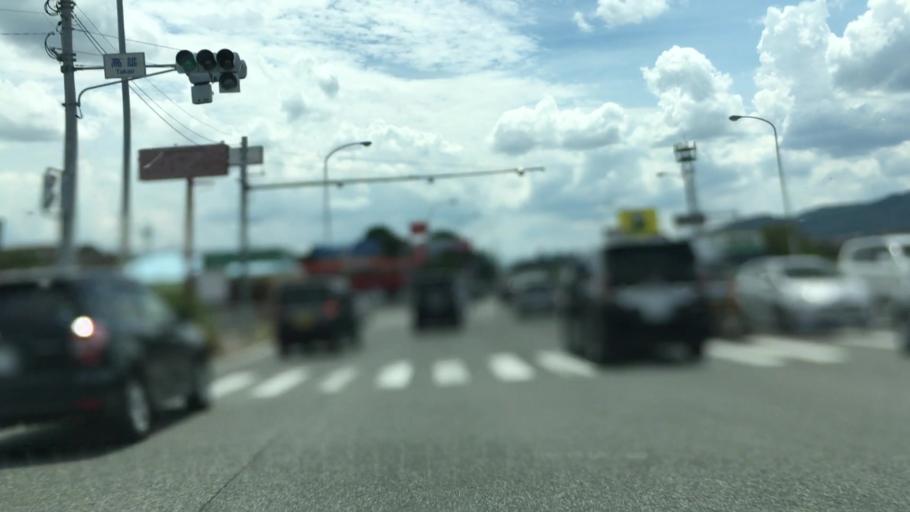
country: JP
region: Fukuoka
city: Chikushino-shi
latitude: 33.4944
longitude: 130.5357
